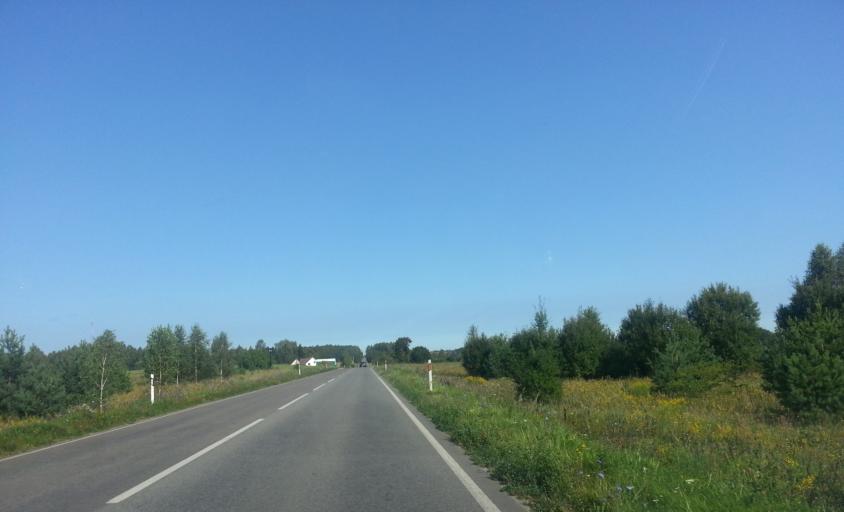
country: LT
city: Grigiskes
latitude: 54.7602
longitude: 25.0811
